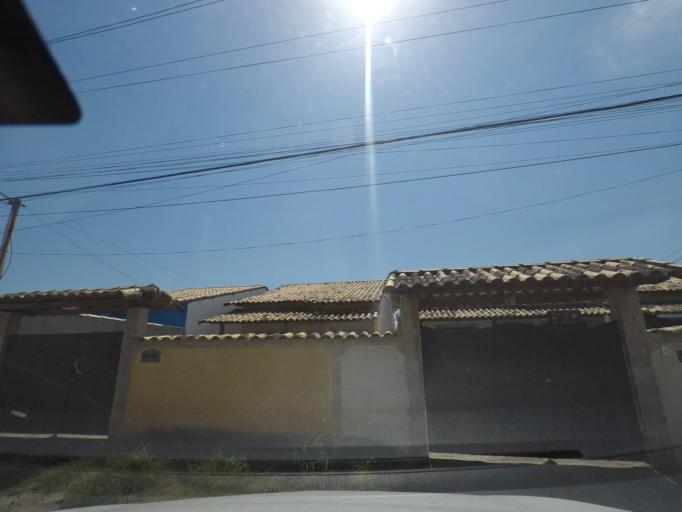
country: BR
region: Rio de Janeiro
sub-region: Marica
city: Marica
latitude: -22.9582
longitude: -42.9649
